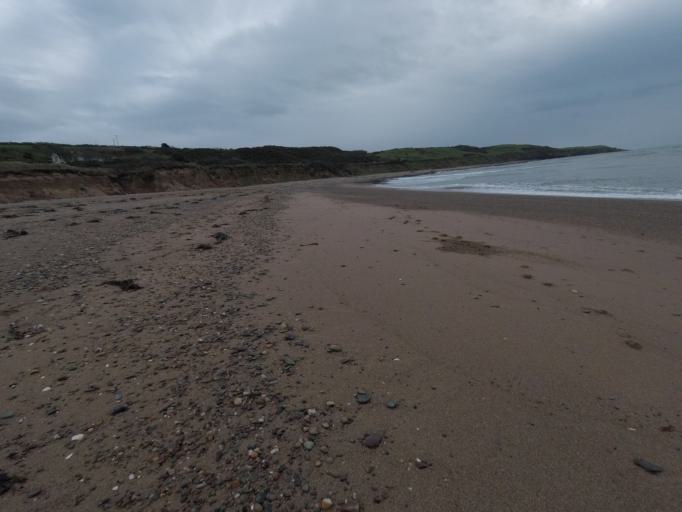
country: IE
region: Munster
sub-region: Waterford
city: Tra Mhor
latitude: 52.1456
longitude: -7.0909
